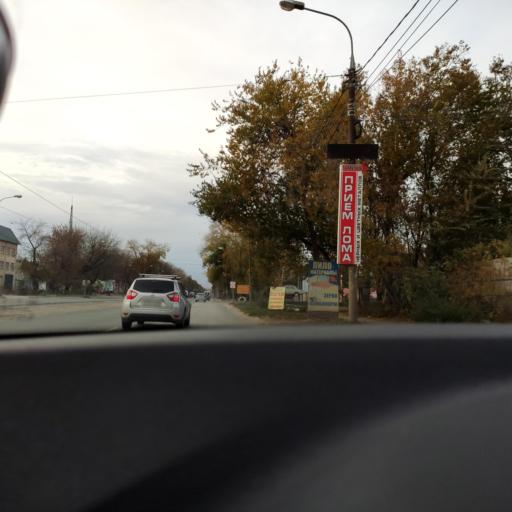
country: RU
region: Samara
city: Smyshlyayevka
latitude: 53.1935
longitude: 50.2932
